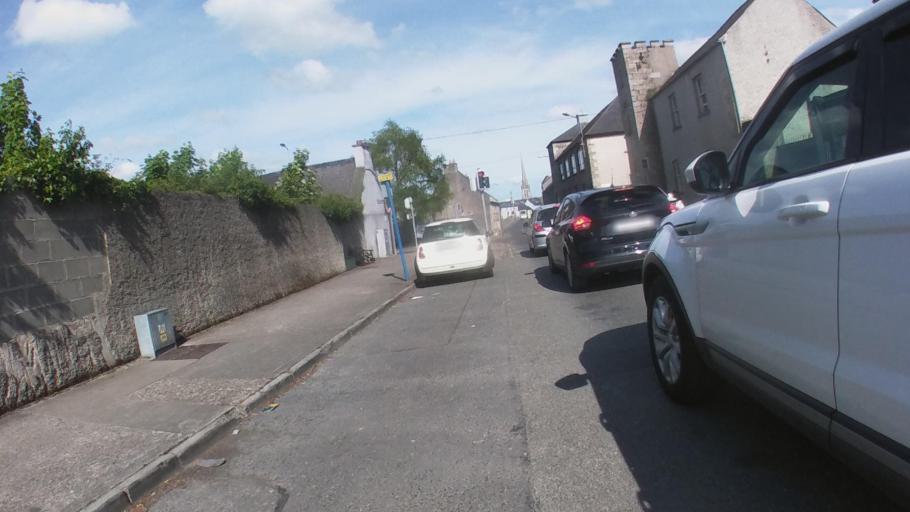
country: IE
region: Leinster
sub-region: County Carlow
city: Carlow
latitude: 52.8367
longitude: -6.9400
